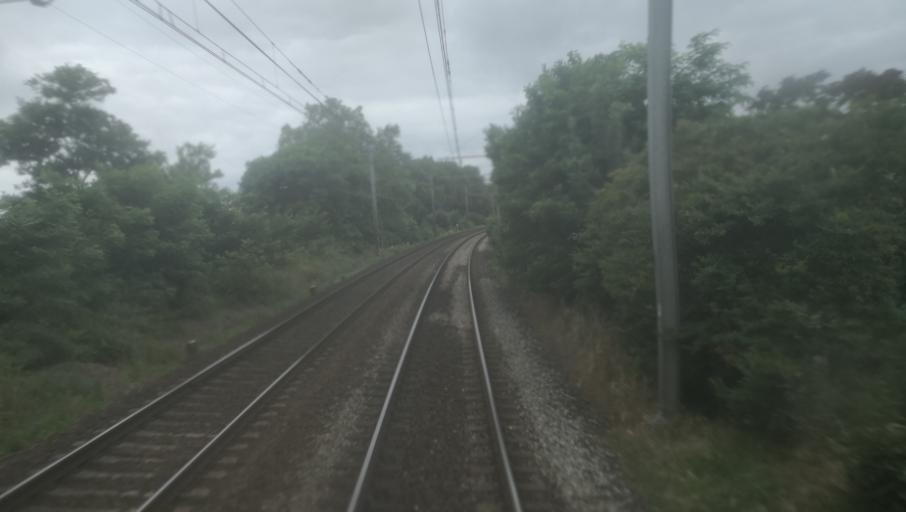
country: FR
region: Midi-Pyrenees
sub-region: Departement de la Haute-Garonne
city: Saint-Jory
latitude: 43.7428
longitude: 1.3670
